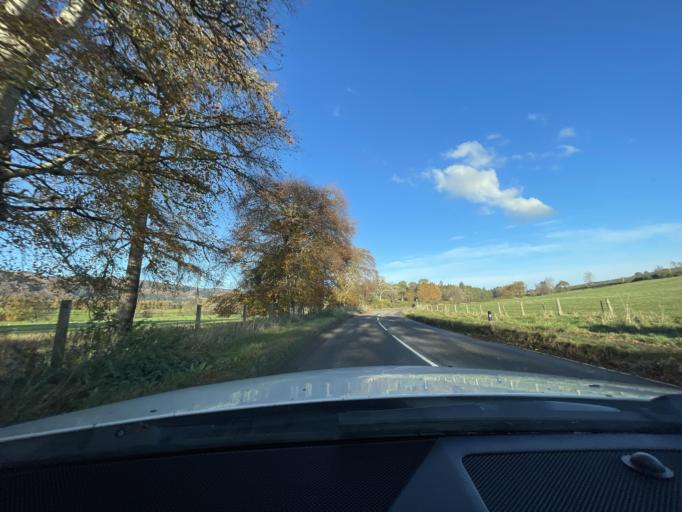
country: GB
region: Scotland
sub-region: Highland
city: Inverness
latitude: 57.3896
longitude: -4.3279
